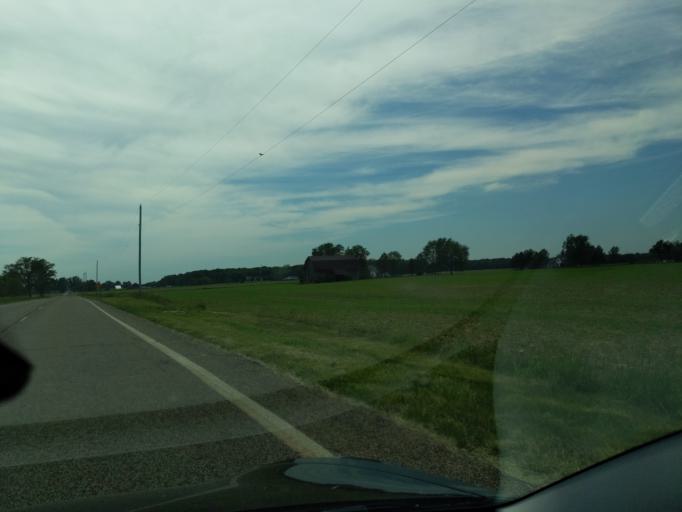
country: US
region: Michigan
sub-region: Barry County
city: Nashville
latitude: 42.7126
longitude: -85.0307
